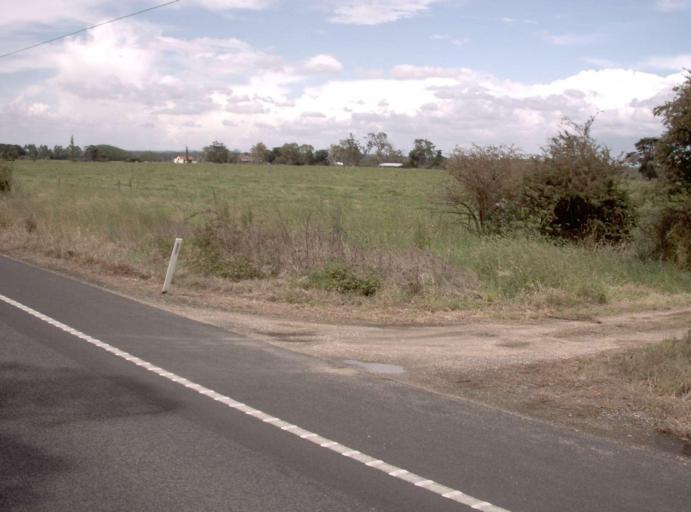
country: AU
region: Victoria
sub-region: Wellington
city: Sale
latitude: -38.0475
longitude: 147.0219
